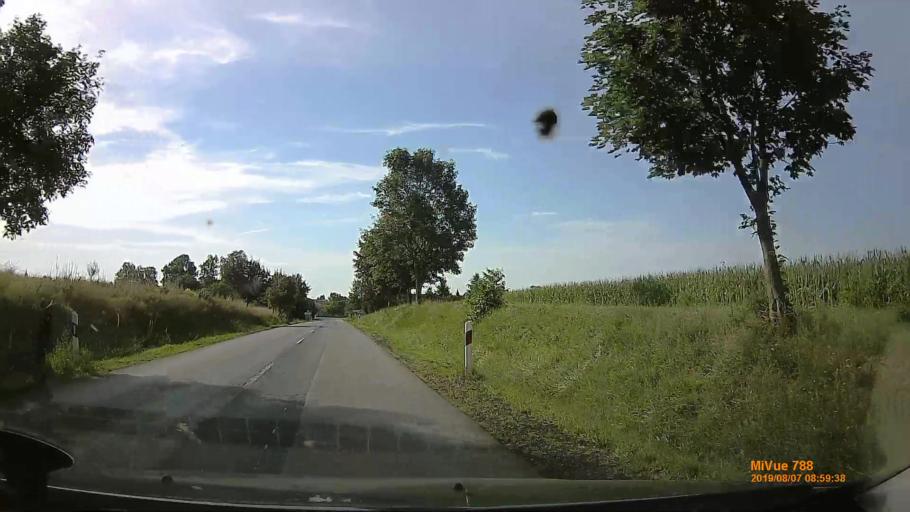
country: HU
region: Zala
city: Pacsa
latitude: 46.7329
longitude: 16.9399
